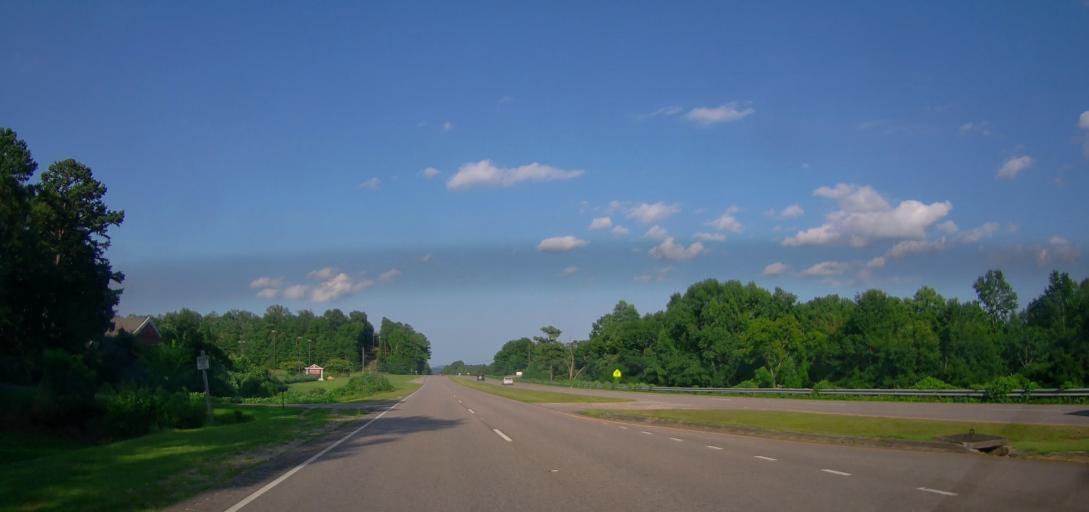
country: US
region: Alabama
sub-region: Jefferson County
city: Irondale
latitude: 33.5480
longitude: -86.6488
